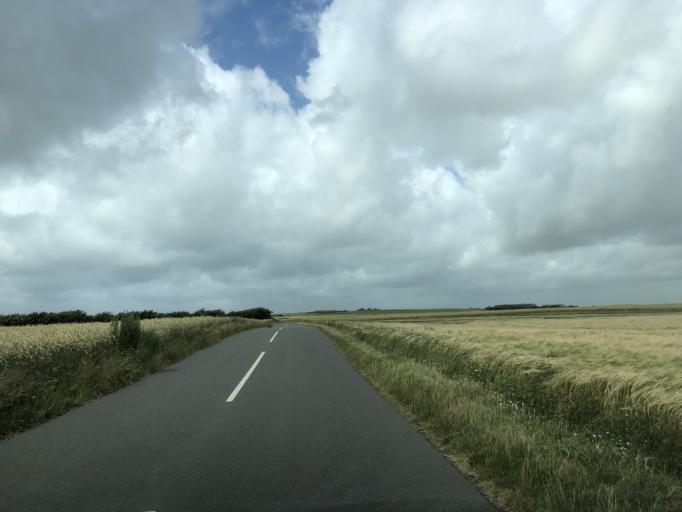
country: DK
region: Central Jutland
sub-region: Lemvig Kommune
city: Harboore
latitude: 56.4943
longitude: 8.1326
